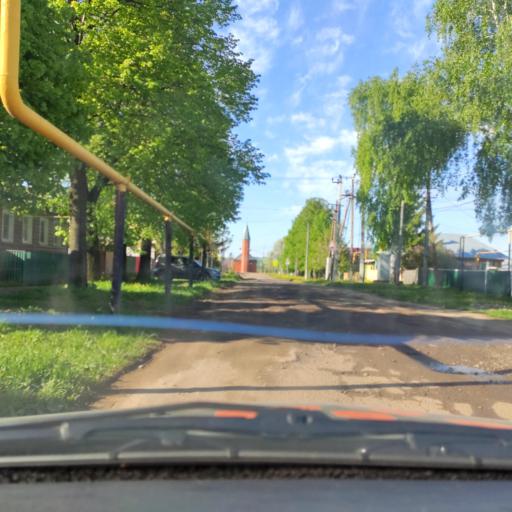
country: RU
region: Bashkortostan
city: Blagoveshchensk
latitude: 54.9461
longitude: 56.1156
